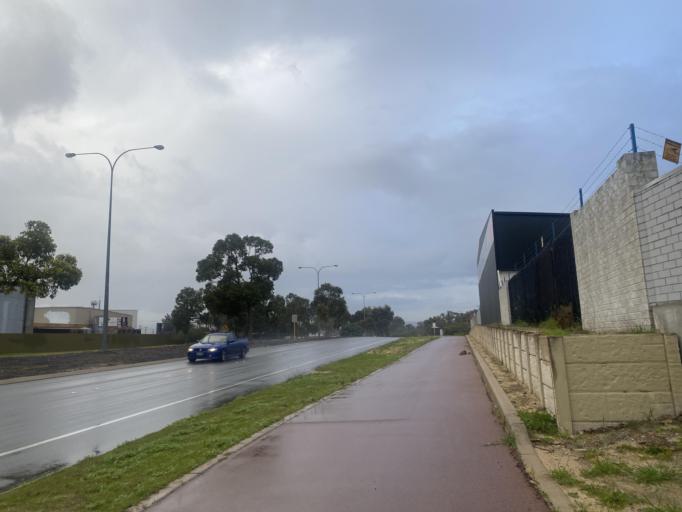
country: AU
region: Western Australia
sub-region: Canning
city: East Cannington
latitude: -32.0007
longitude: 115.9675
